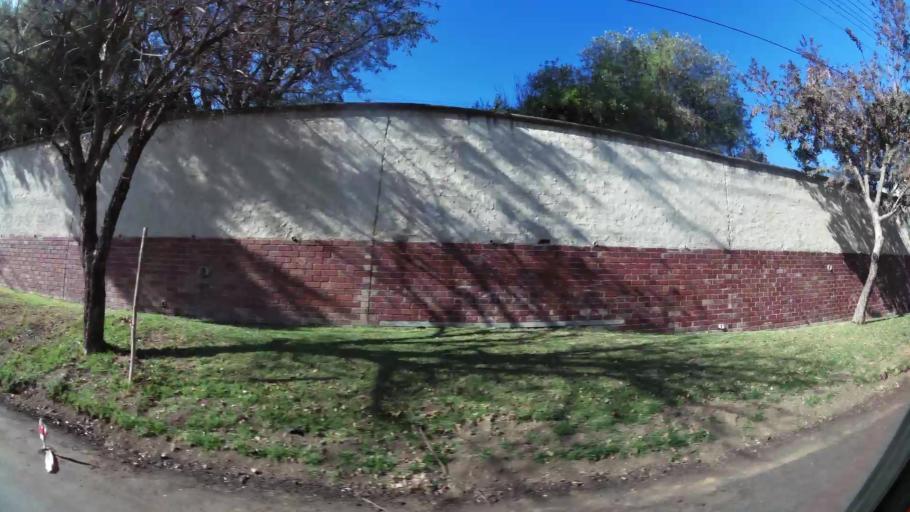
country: ZA
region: Gauteng
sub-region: City of Johannesburg Metropolitan Municipality
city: Johannesburg
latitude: -26.1221
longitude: 28.0184
